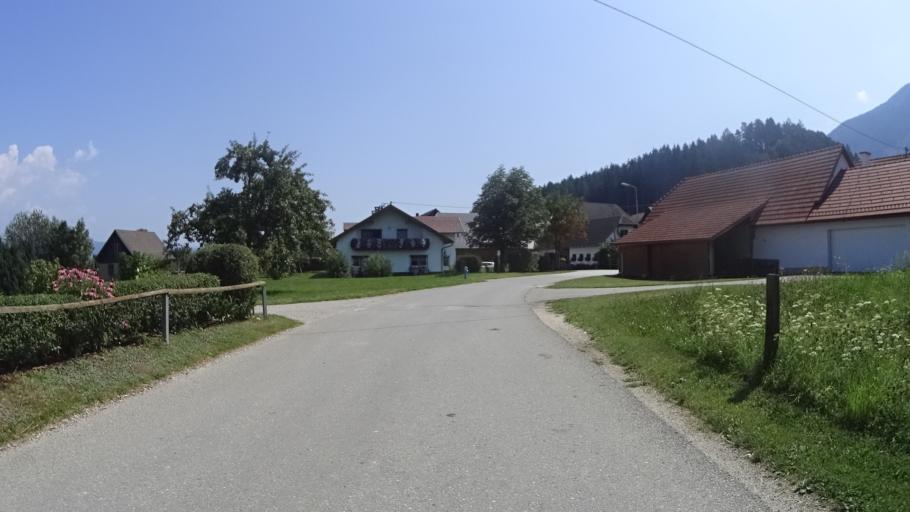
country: AT
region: Carinthia
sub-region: Politischer Bezirk Volkermarkt
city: Globasnitz
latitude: 46.5554
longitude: 14.7215
